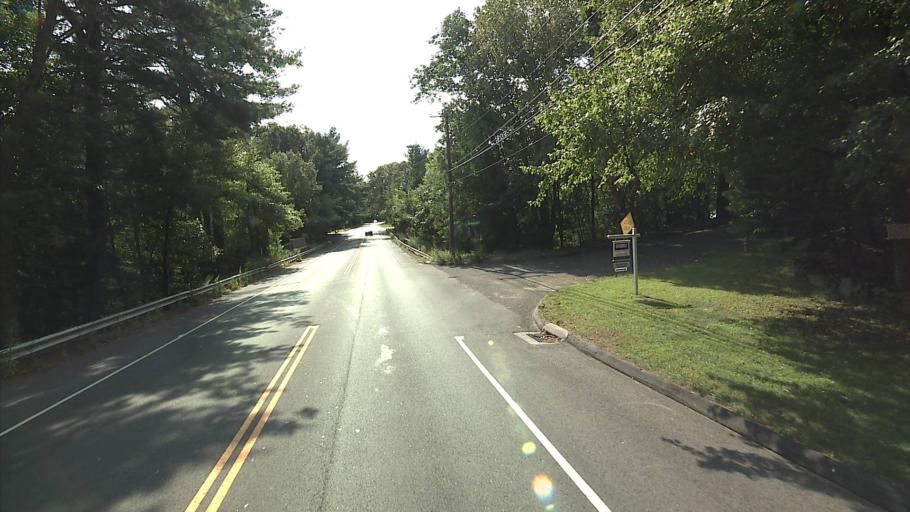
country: US
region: Connecticut
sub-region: Fairfield County
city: Fairfield
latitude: 41.1928
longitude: -73.2606
